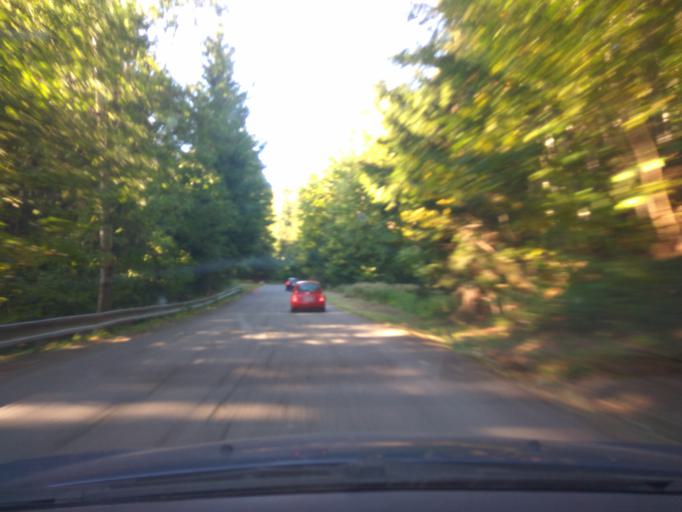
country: SK
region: Banskobystricky
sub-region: Okres Ziar nad Hronom
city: Kremnica
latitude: 48.7257
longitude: 18.9883
